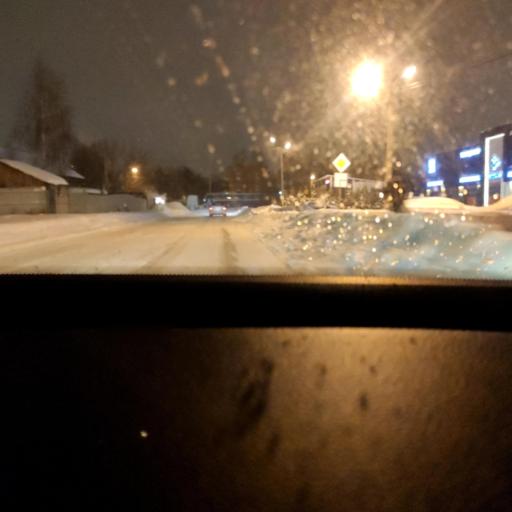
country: RU
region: Moskovskaya
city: Odintsovo
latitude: 55.6652
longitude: 37.2652
